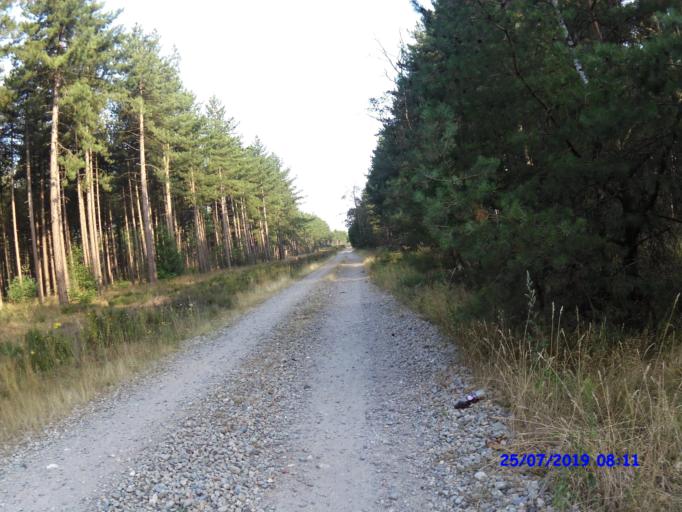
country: BE
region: Flanders
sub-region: Provincie Limburg
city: Lommel
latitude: 51.1755
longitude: 5.3106
